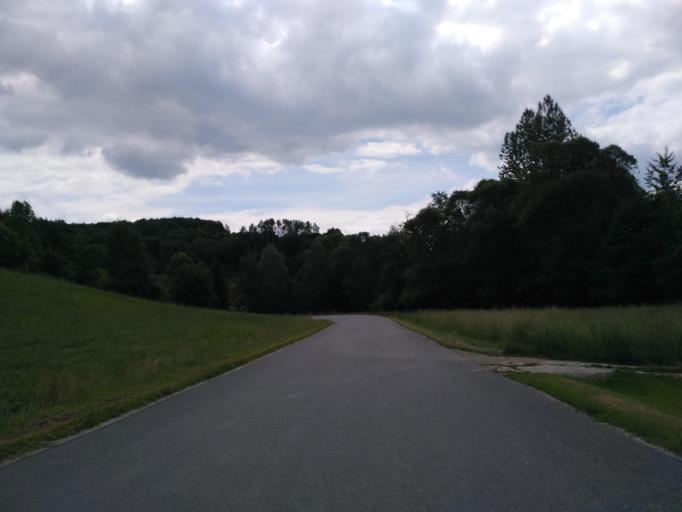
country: PL
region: Subcarpathian Voivodeship
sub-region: Powiat przeworski
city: Jawornik Polski
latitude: 49.8495
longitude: 22.3035
